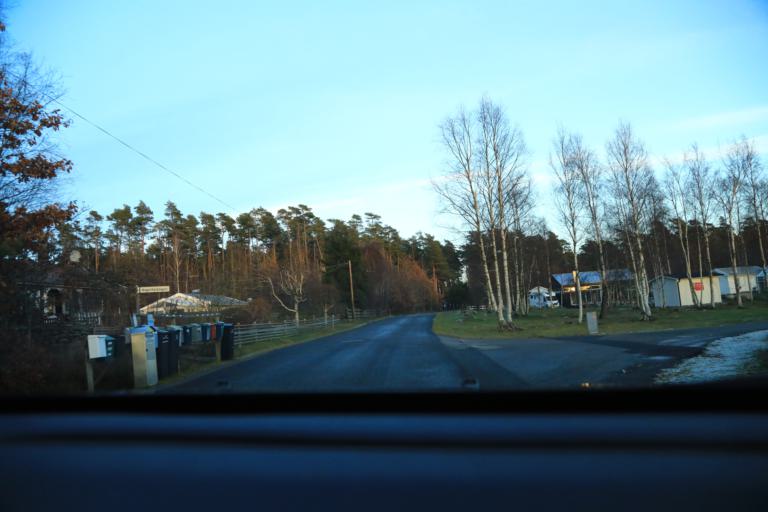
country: SE
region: Halland
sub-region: Varbergs Kommun
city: Varberg
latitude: 57.1941
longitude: 12.1879
